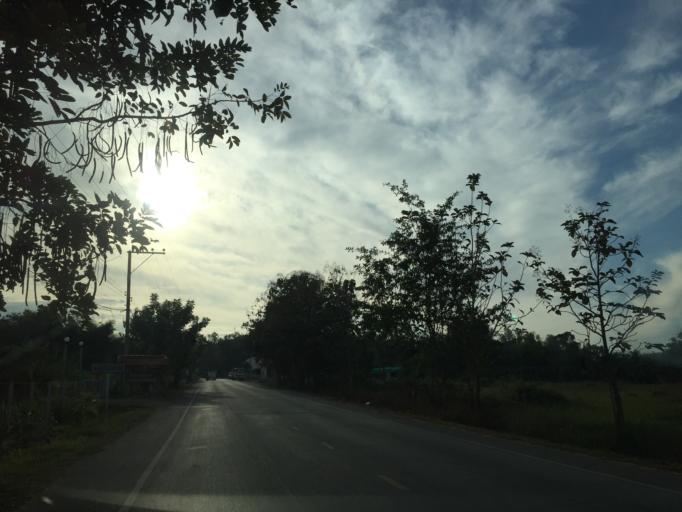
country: TH
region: Lamphun
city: Lamphun
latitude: 18.5125
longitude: 99.0262
